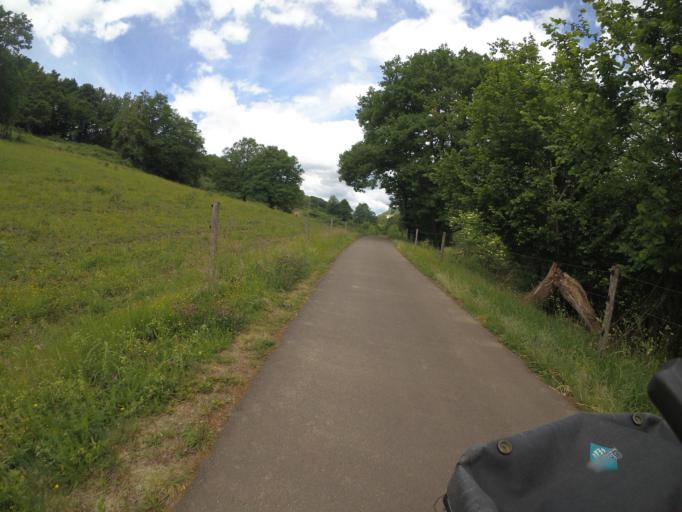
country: DE
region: Rheinland-Pfalz
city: Niederstaufenbach
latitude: 49.5378
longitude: 7.5074
